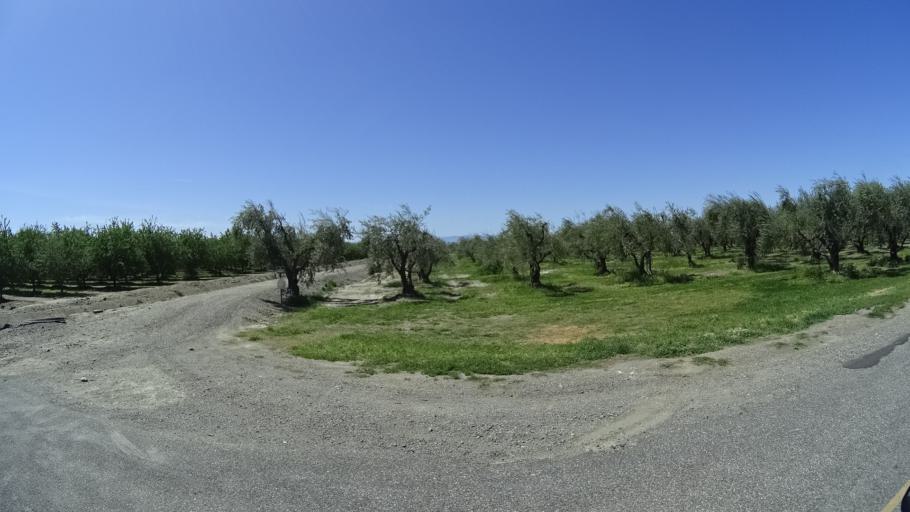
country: US
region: California
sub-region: Glenn County
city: Orland
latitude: 39.7434
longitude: -122.1595
